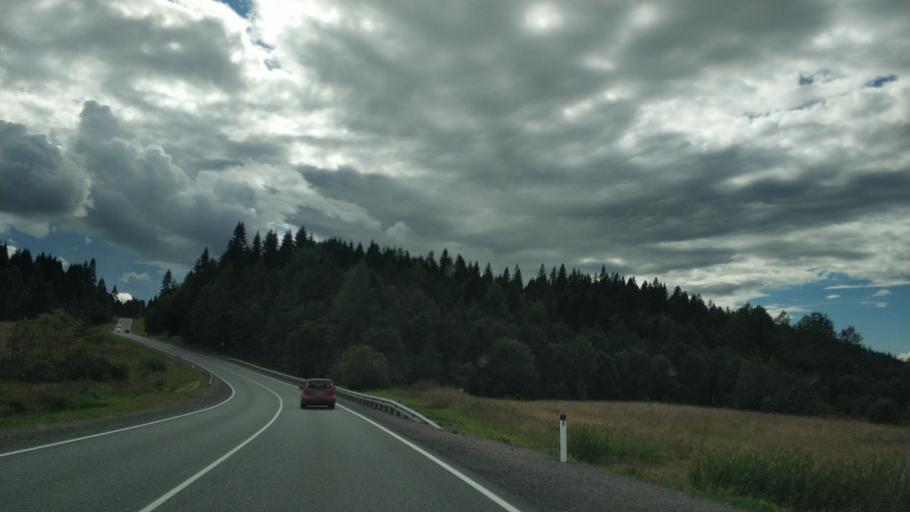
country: RU
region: Republic of Karelia
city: Khelyulya
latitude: 61.7731
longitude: 30.6559
